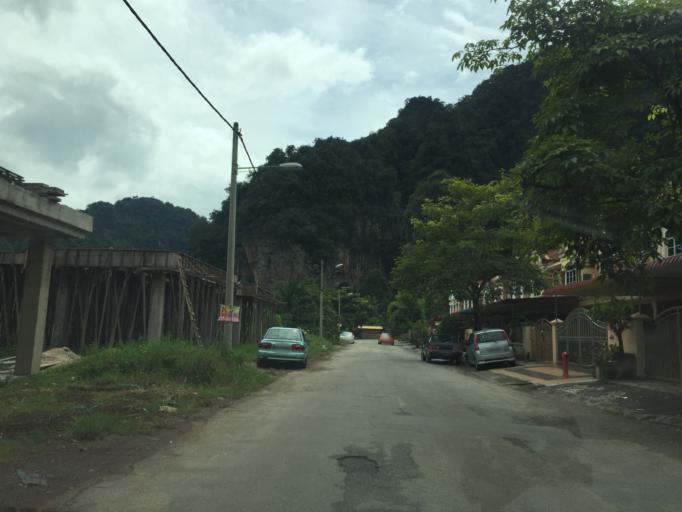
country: MY
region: Perak
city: Ipoh
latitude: 4.5631
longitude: 101.1239
